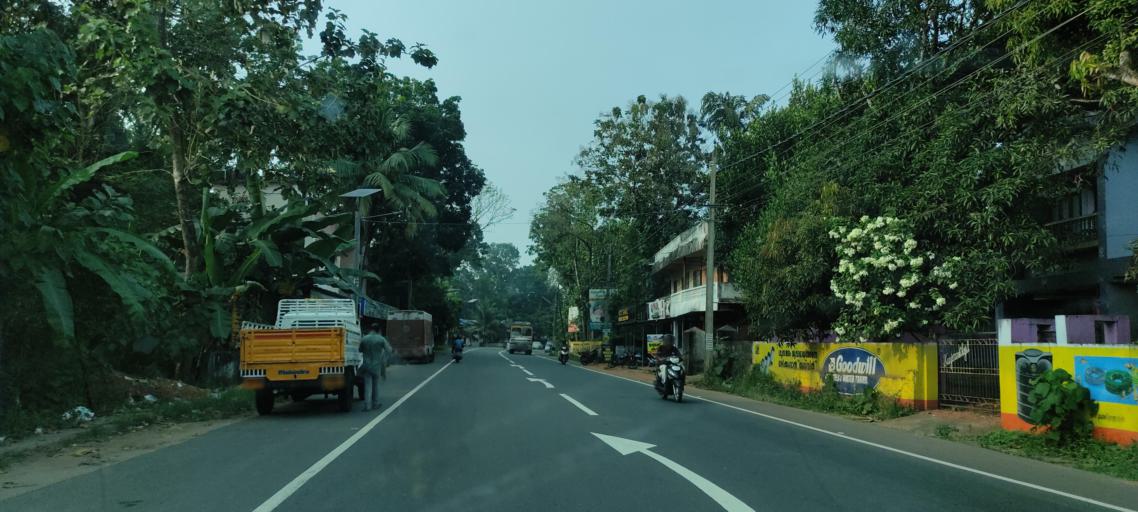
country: IN
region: Kerala
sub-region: Pattanamtitta
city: Adur
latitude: 9.1001
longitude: 76.7511
